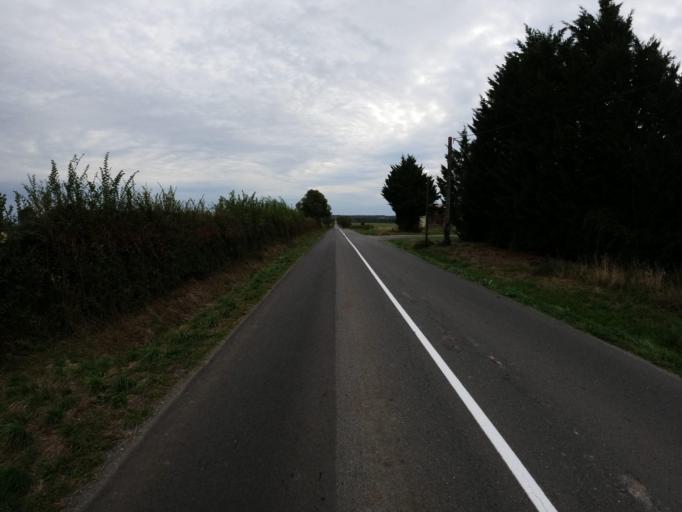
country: FR
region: Poitou-Charentes
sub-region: Departement de la Vienne
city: Saulge
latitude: 46.3833
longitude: 0.8482
